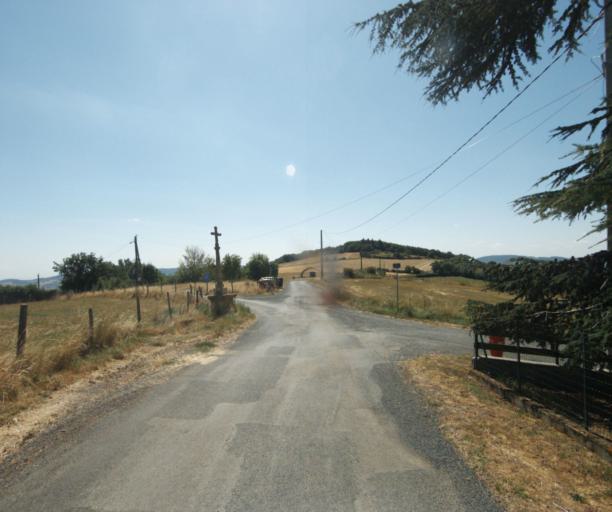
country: FR
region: Rhone-Alpes
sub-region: Departement du Rhone
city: Bessenay
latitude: 45.8069
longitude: 4.5284
